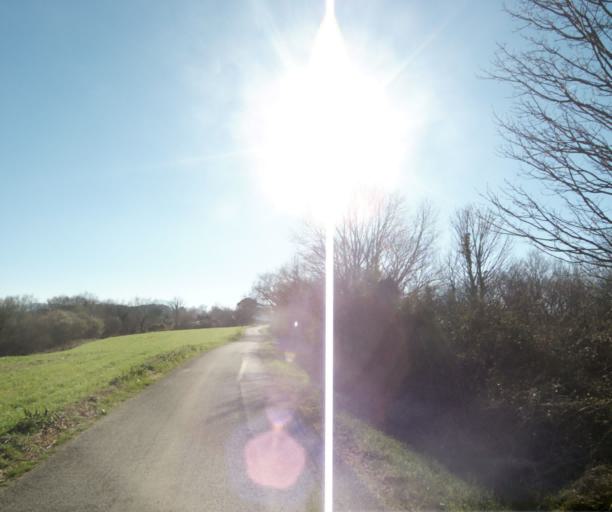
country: FR
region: Aquitaine
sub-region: Departement des Pyrenees-Atlantiques
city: Hendaye
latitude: 43.3614
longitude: -1.7372
